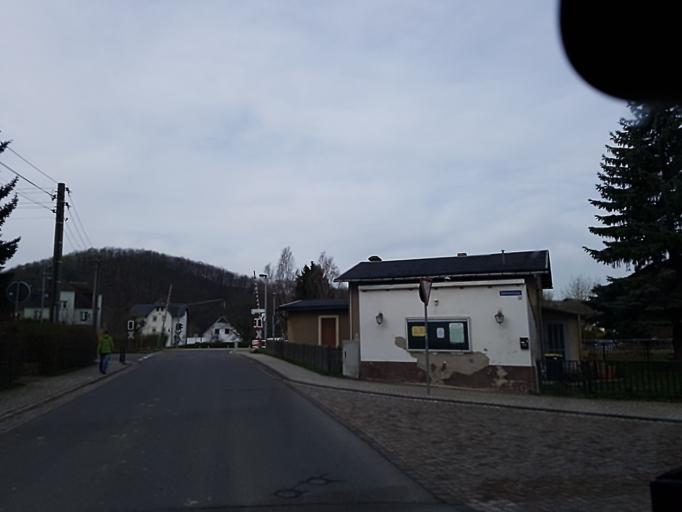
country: DE
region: Saxony
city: Grossweitzschen
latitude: 51.1373
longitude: 13.0288
